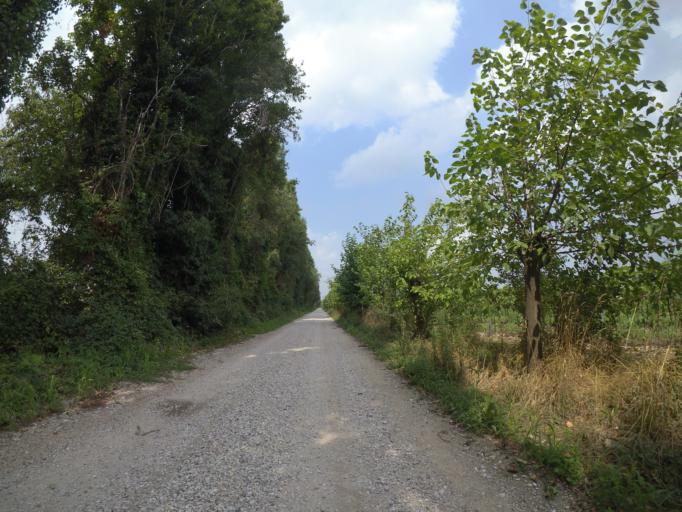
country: IT
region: Friuli Venezia Giulia
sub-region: Provincia di Udine
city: Sedegliano
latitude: 46.0055
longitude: 13.0107
